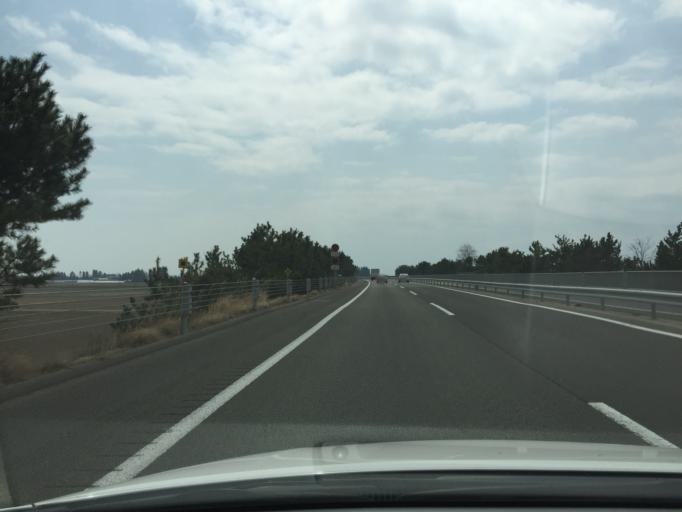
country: JP
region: Miyagi
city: Iwanuma
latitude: 38.1227
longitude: 140.8868
